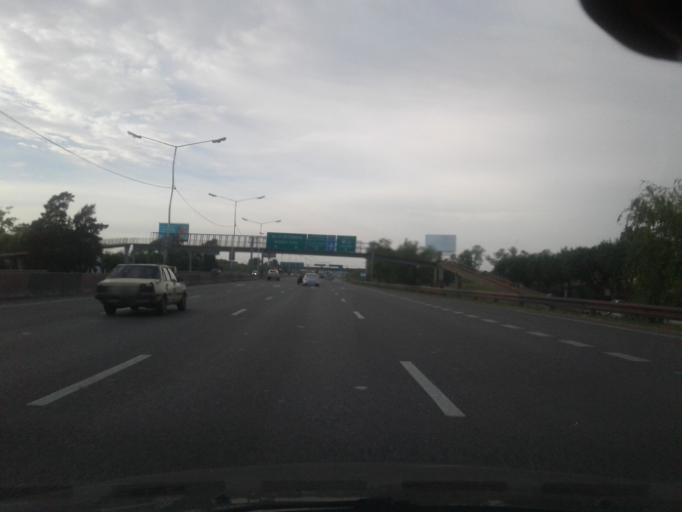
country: AR
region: Santa Fe
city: Perez
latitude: -32.9441
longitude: -60.7225
